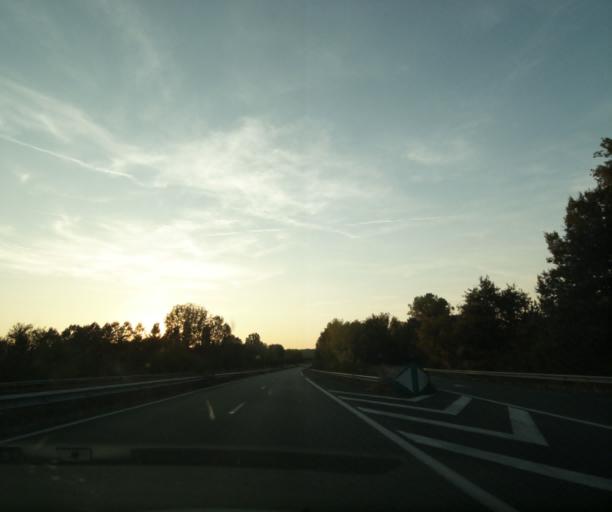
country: FR
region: Aquitaine
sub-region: Departement du Lot-et-Garonne
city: Fourques-sur-Garonne
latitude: 44.4294
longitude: 0.1389
